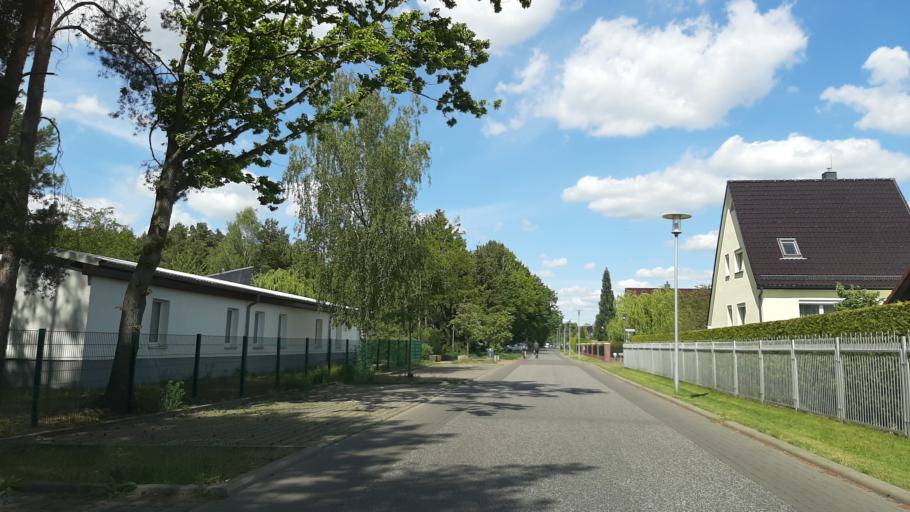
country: DE
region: Brandenburg
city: Hennigsdorf
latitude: 52.6482
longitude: 13.1894
